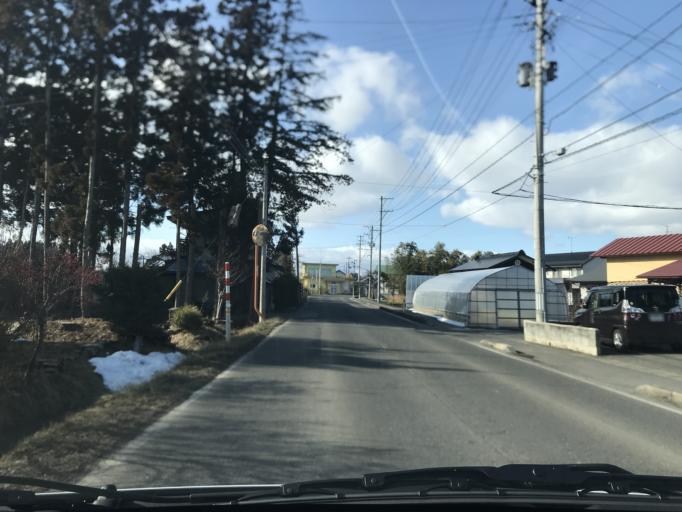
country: JP
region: Iwate
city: Kitakami
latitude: 39.3003
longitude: 141.1060
